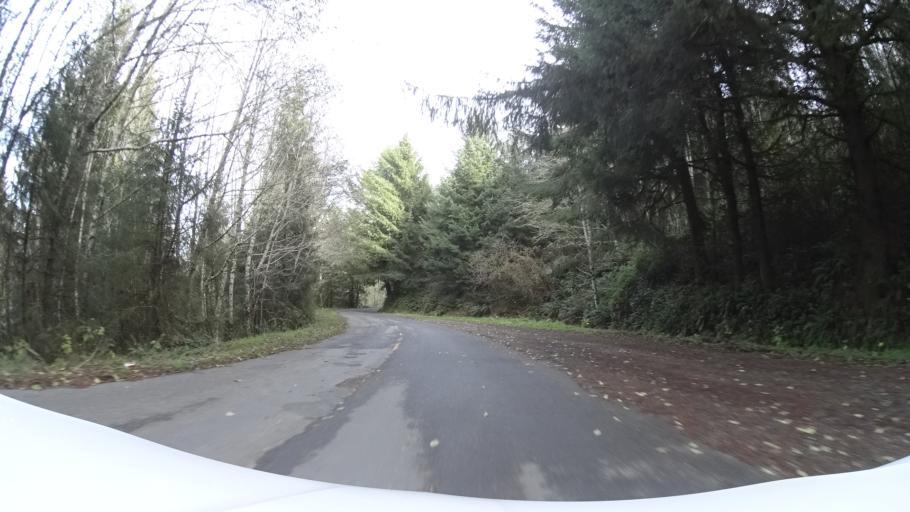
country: US
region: California
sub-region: Humboldt County
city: Ferndale
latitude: 40.5425
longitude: -124.2779
